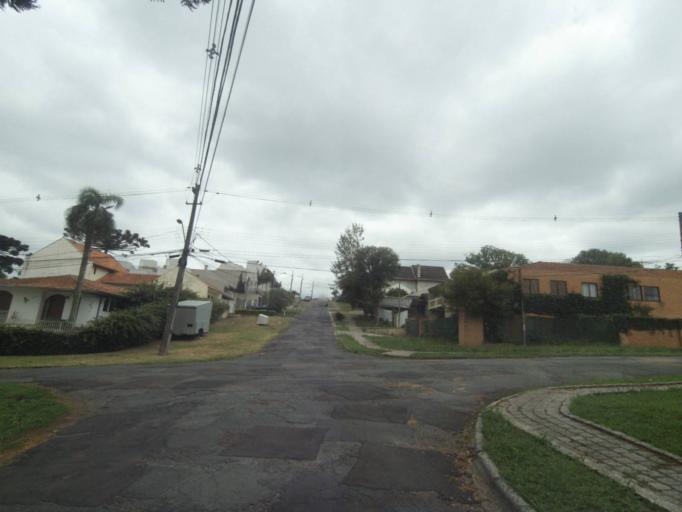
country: BR
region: Parana
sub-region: Curitiba
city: Curitiba
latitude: -25.3897
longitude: -49.2771
